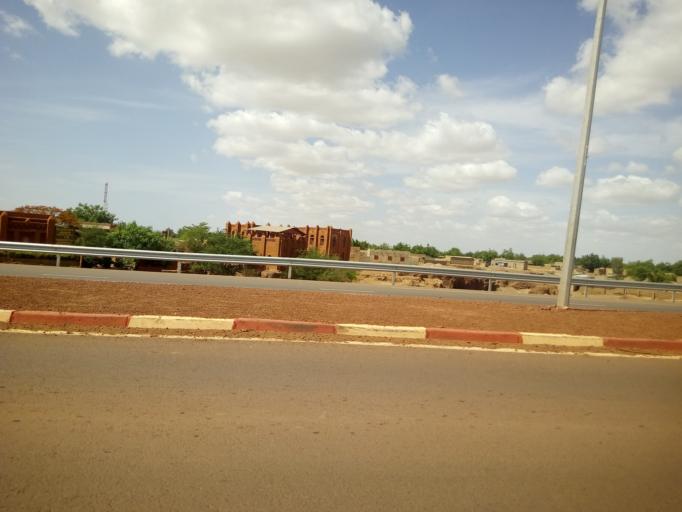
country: ML
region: Segou
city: Segou
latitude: 13.4270
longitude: -6.2203
